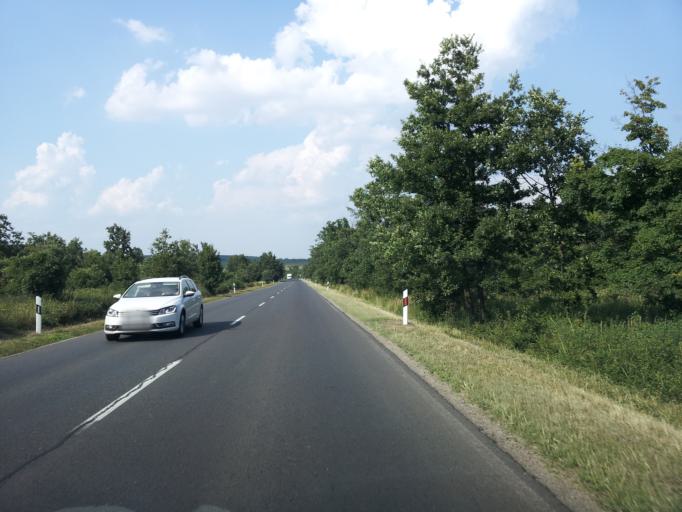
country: HU
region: Veszprem
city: Nemesvamos
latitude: 47.0302
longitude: 17.9114
